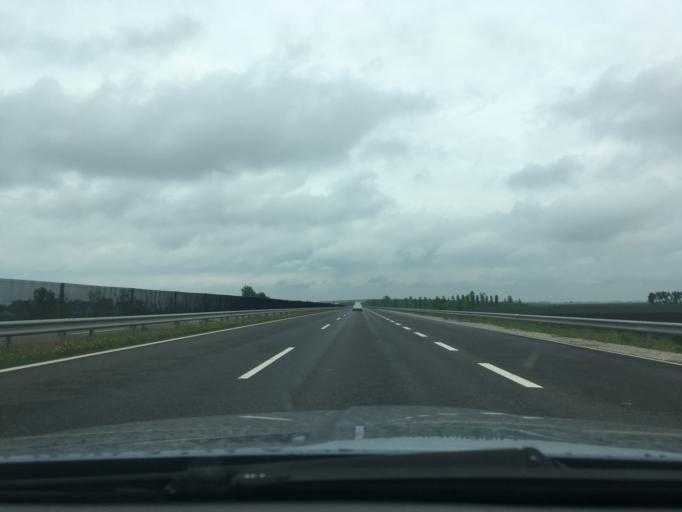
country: HU
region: Hajdu-Bihar
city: Hajduboszormeny
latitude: 47.7040
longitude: 21.4344
